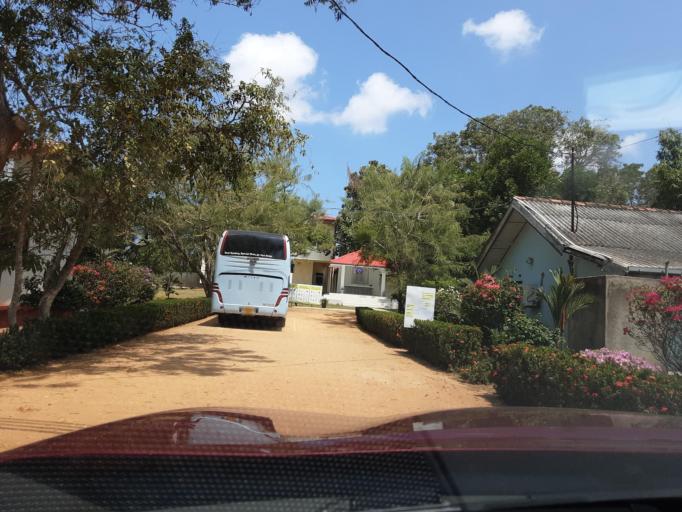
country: LK
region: Southern
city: Tangalla
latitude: 6.2082
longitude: 81.2073
